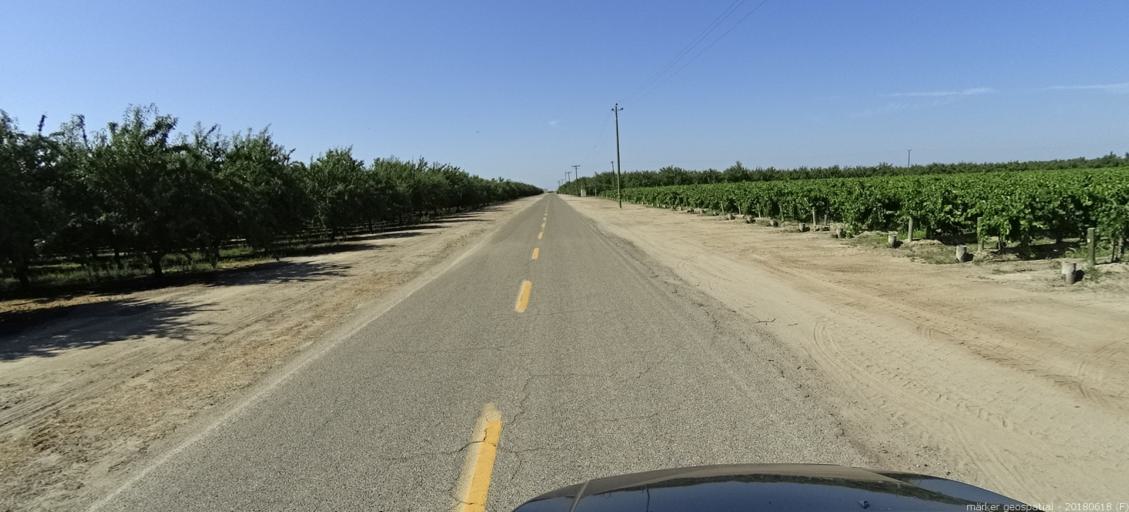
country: US
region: California
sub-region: Madera County
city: Parkwood
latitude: 36.8418
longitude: -120.1464
